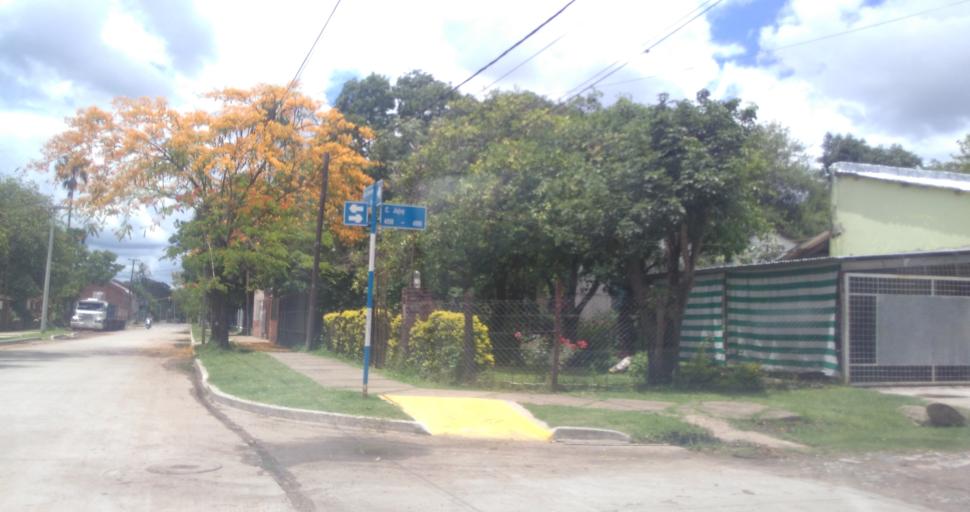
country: AR
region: Chaco
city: Fontana
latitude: -27.4191
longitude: -59.0332
